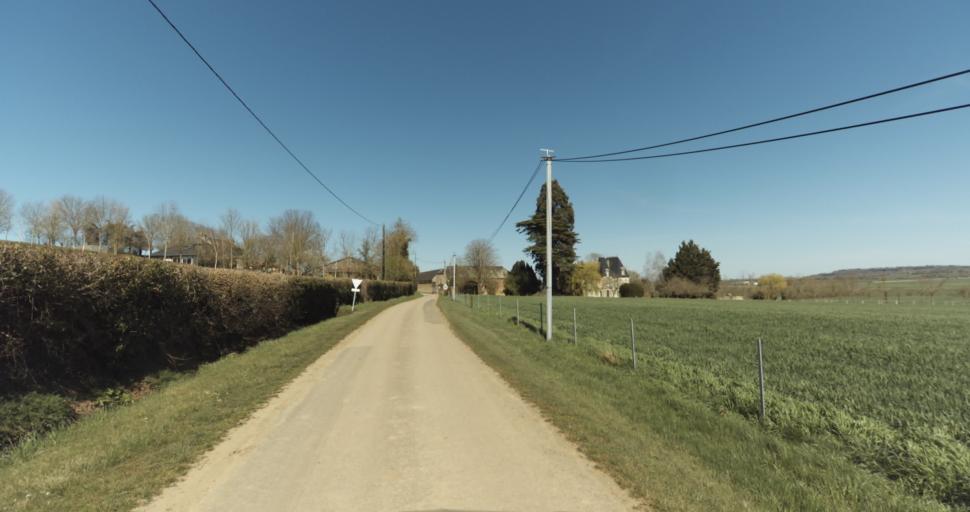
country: FR
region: Lower Normandy
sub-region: Departement du Calvados
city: Saint-Pierre-sur-Dives
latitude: 49.0163
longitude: 0.0140
